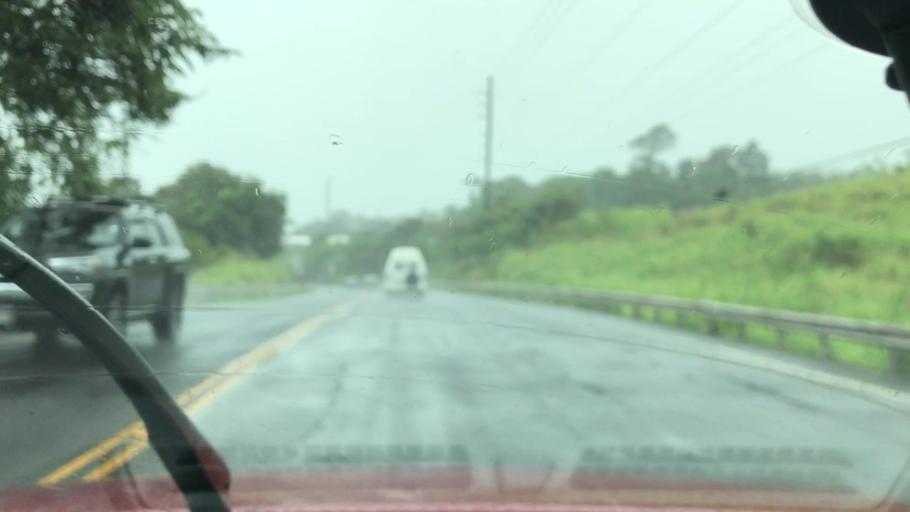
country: US
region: Hawaii
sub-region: Hawaii County
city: Pepeekeo
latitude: 19.9873
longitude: -155.2427
